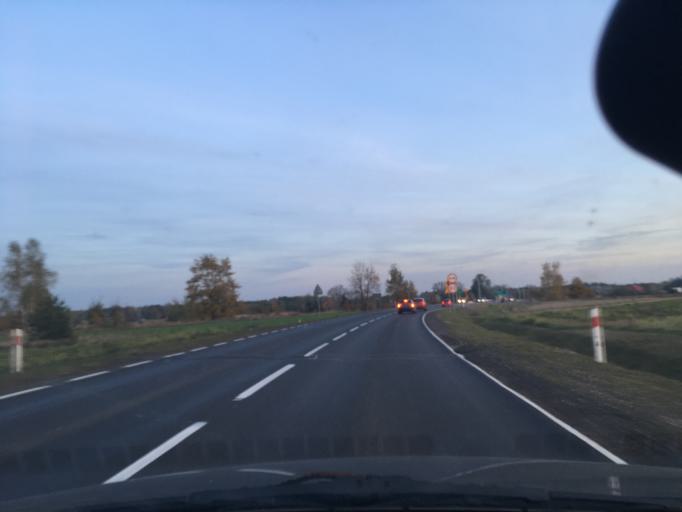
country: PL
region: Masovian Voivodeship
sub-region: Powiat plocki
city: Wyszogrod
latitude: 52.3591
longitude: 20.2060
